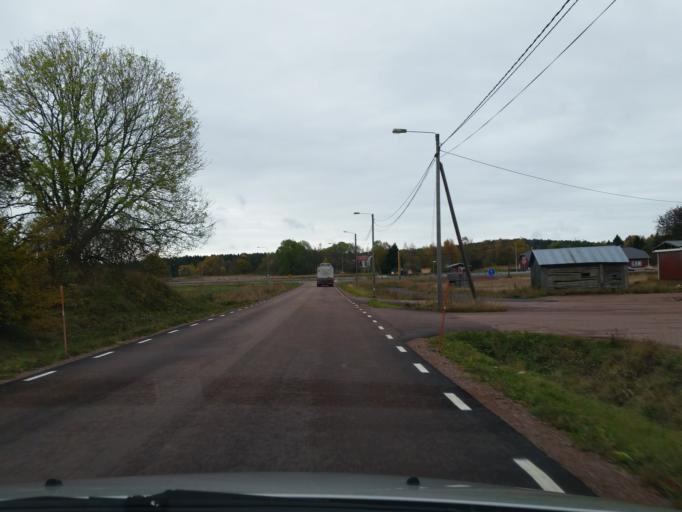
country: AX
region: Alands landsbygd
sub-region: Lemland
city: Lemland
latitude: 60.0706
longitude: 20.0854
